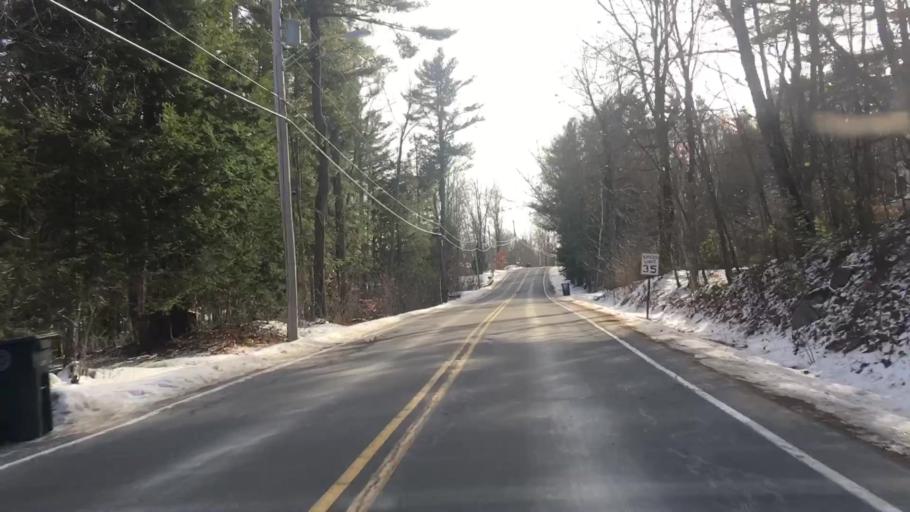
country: US
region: Maine
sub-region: Cumberland County
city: Westbrook
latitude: 43.7236
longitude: -70.3572
